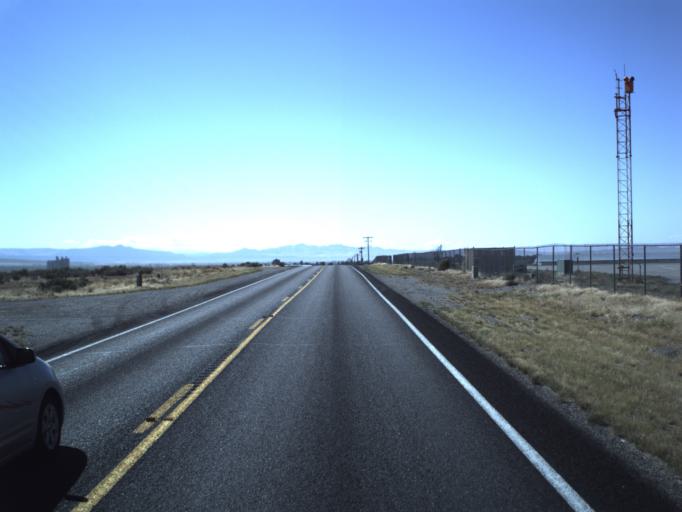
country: US
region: Utah
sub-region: Beaver County
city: Milford
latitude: 38.4199
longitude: -113.0099
